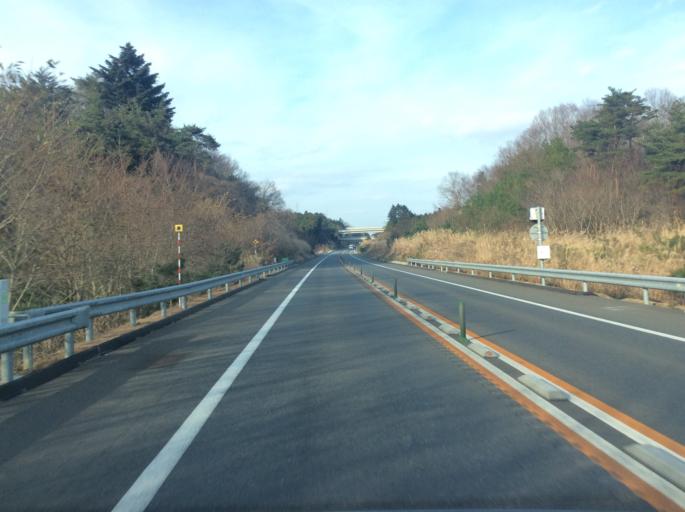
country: JP
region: Fukushima
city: Namie
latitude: 37.3219
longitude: 140.9910
